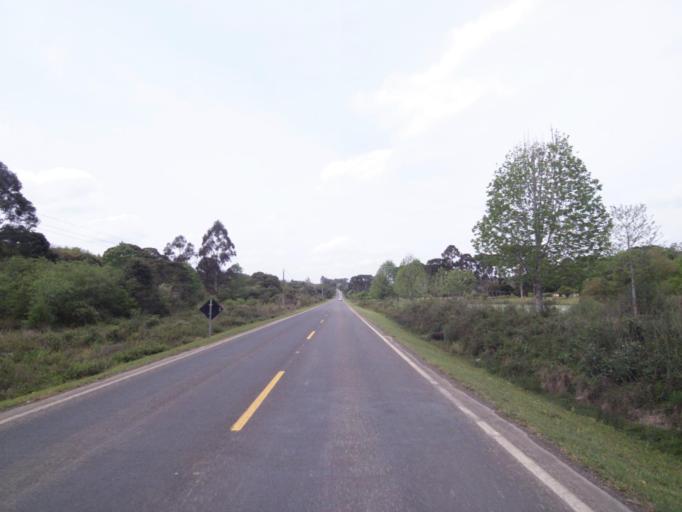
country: BR
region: Parana
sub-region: Irati
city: Irati
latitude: -25.4599
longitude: -50.5683
